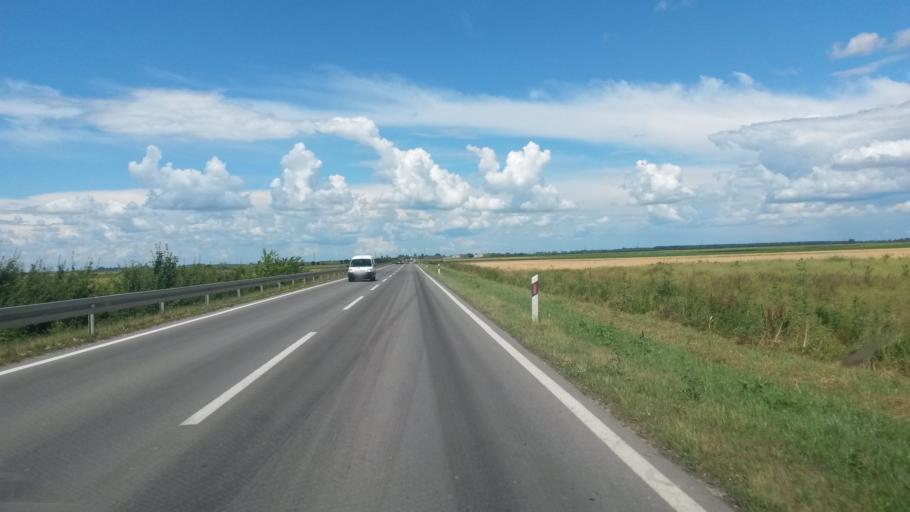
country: HR
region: Osjecko-Baranjska
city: Vladislavci
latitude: 45.4785
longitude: 18.5388
